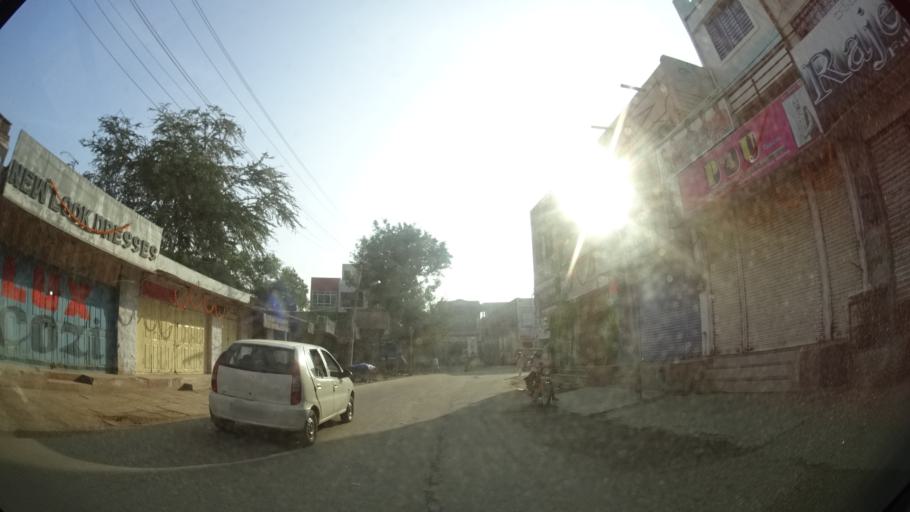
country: IN
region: Karnataka
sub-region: Bellary
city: Hospet
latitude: 15.2722
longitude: 76.3930
